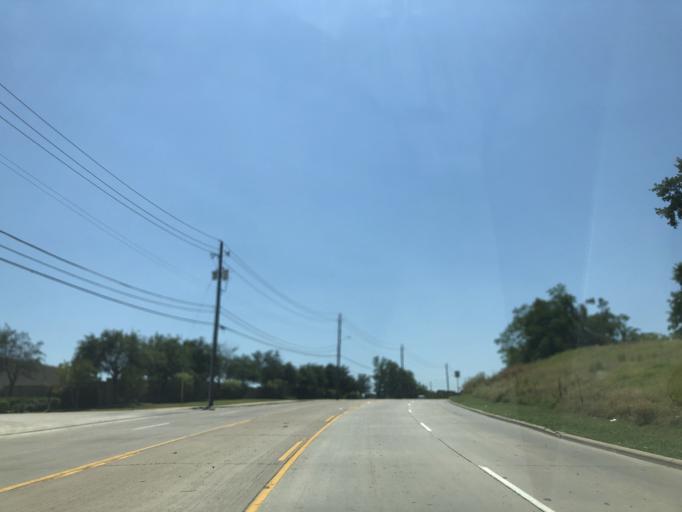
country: US
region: Texas
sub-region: Dallas County
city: Irving
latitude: 32.8310
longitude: -96.8992
